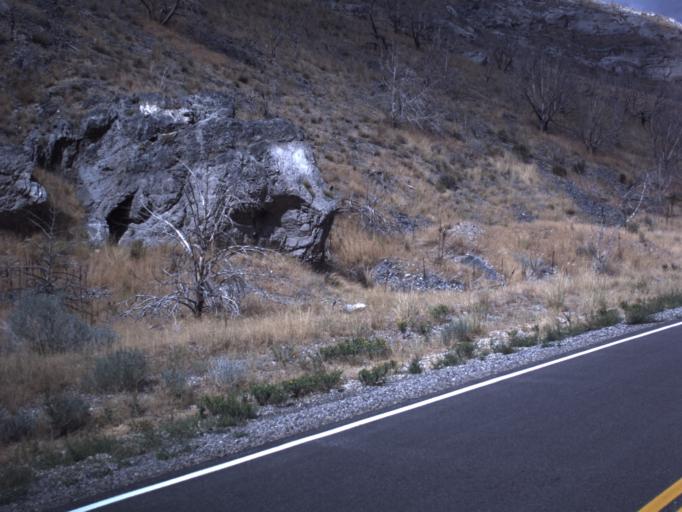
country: US
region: Utah
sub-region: Tooele County
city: Grantsville
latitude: 40.3449
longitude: -112.5957
